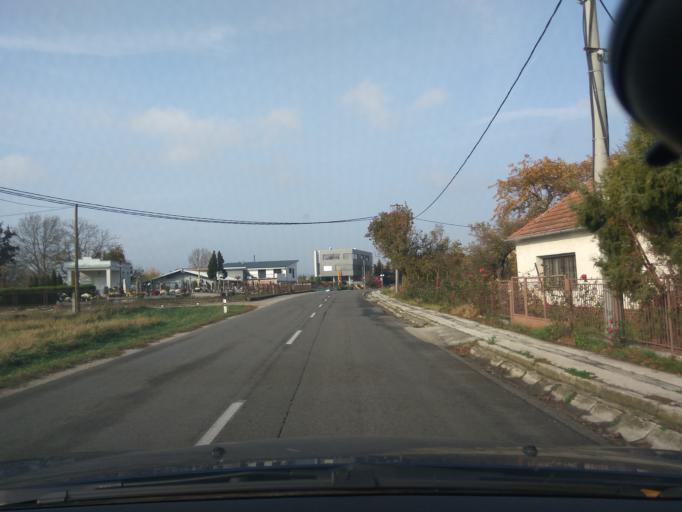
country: SK
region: Trnavsky
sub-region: Okres Trnava
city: Piestany
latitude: 48.6253
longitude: 17.7791
